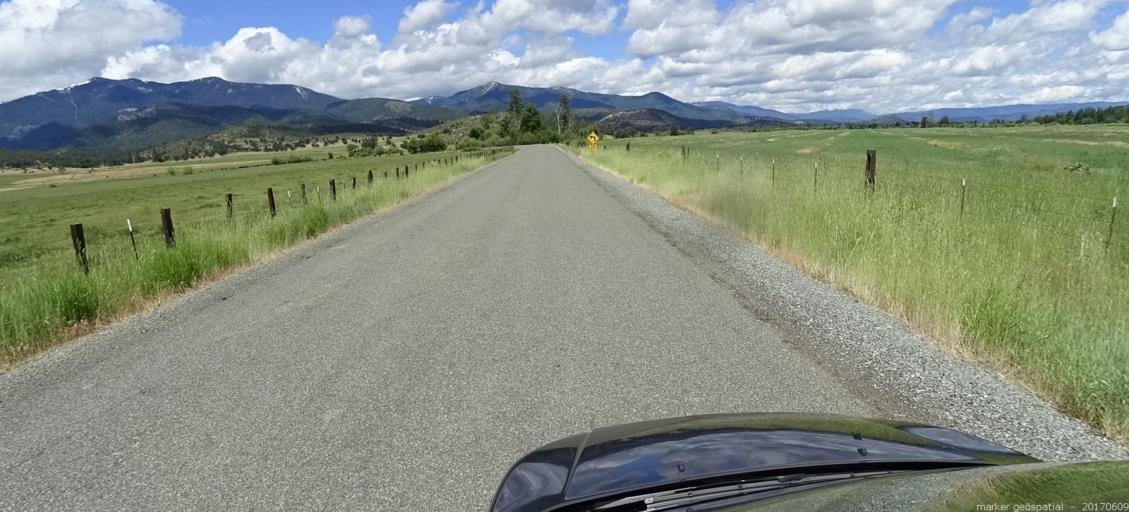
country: US
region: California
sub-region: Siskiyou County
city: Yreka
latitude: 41.3963
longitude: -122.8350
